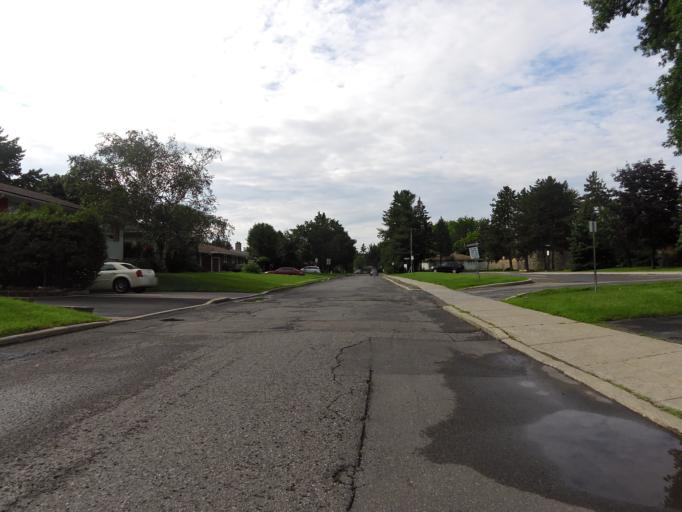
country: CA
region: Ontario
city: Bells Corners
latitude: 45.3375
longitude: -75.7879
